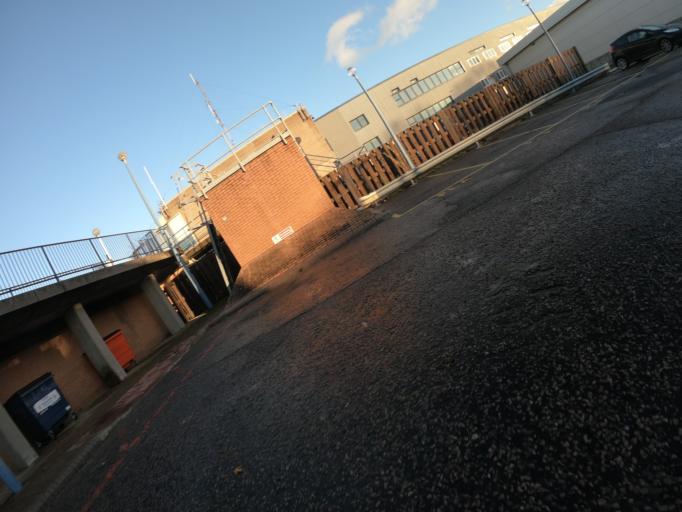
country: GB
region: England
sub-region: Greater London
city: Woolwich
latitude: 51.4953
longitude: 0.0415
